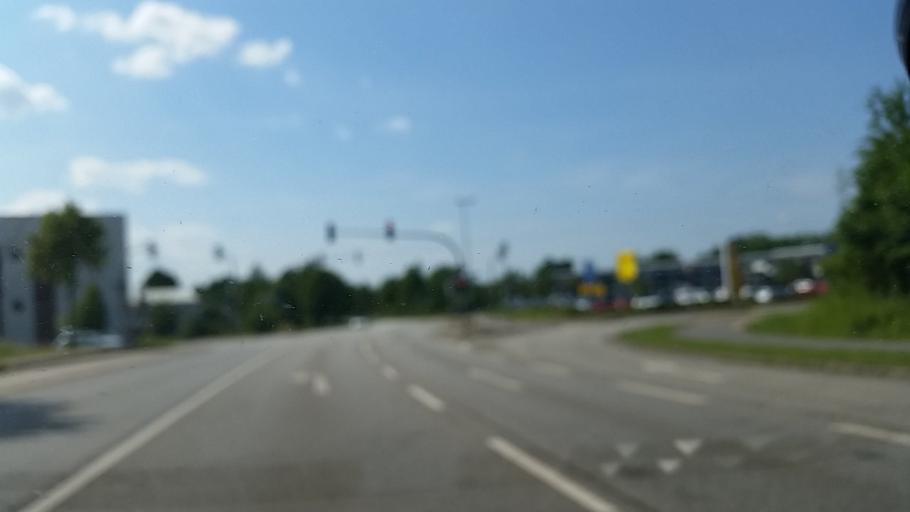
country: DE
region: Schleswig-Holstein
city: Reinbek
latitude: 53.5303
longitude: 10.2385
